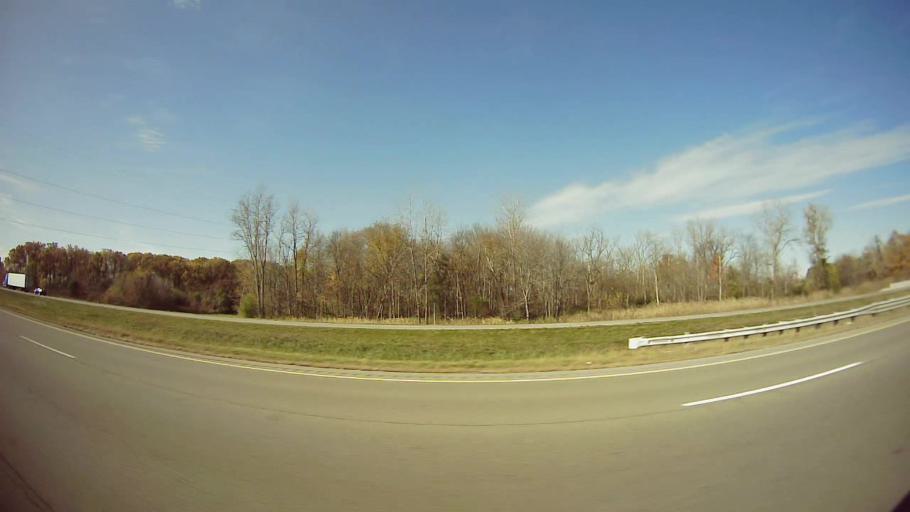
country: US
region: Michigan
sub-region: Wayne County
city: Romulus
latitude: 42.2479
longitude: -83.4397
